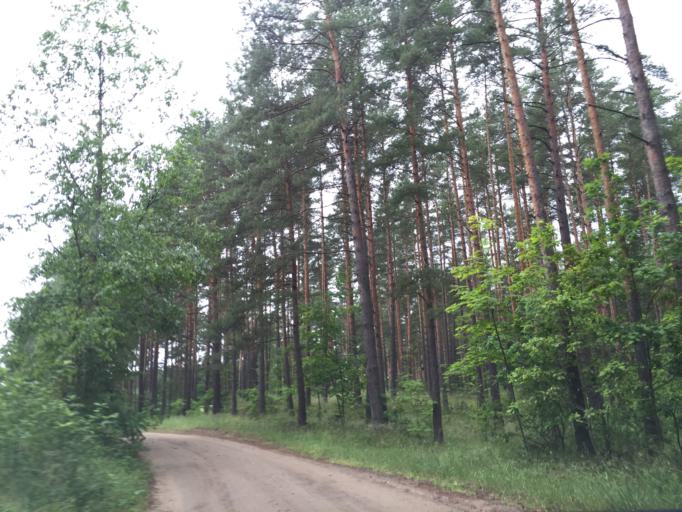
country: LV
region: Riga
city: Jaunciems
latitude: 57.0545
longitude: 24.1768
